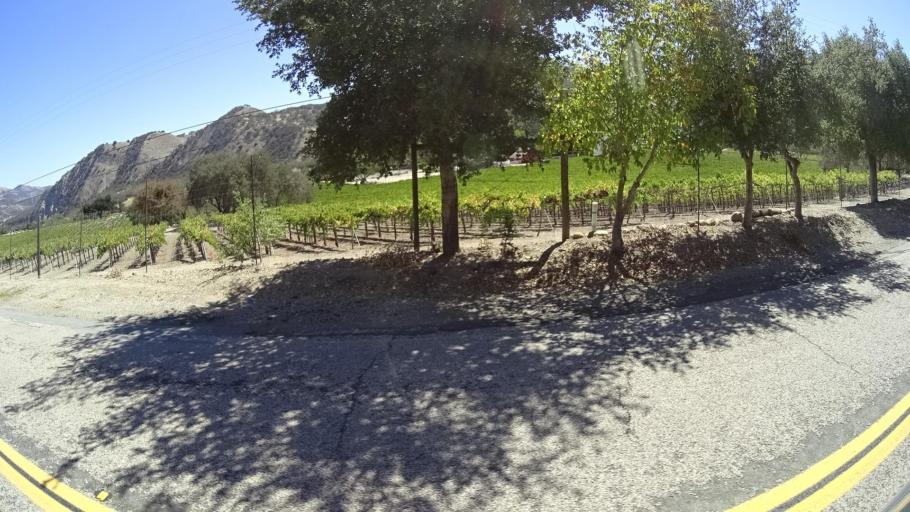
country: US
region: California
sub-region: Monterey County
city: Greenfield
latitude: 36.2597
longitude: -121.4204
